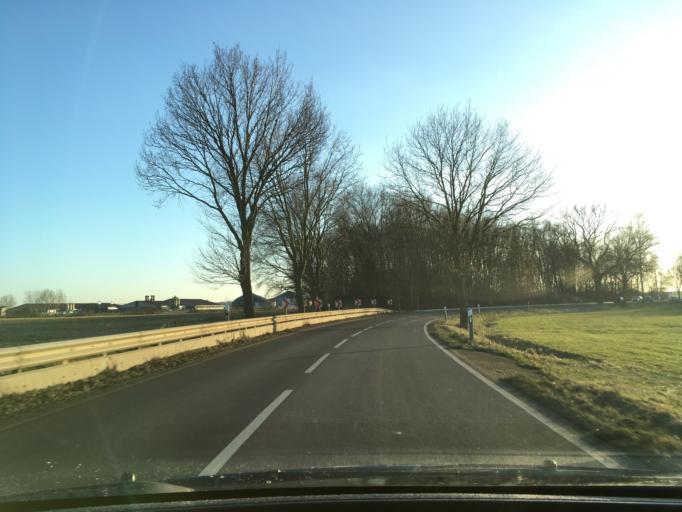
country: DE
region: Lower Saxony
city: Echem
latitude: 53.3314
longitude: 10.5152
